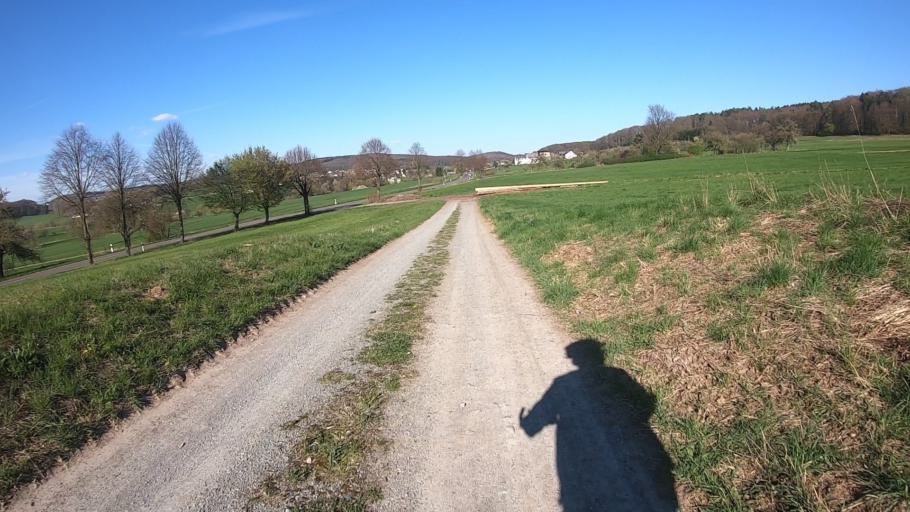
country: DE
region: Rheinland-Pfalz
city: Maxsain
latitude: 50.5388
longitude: 7.7720
